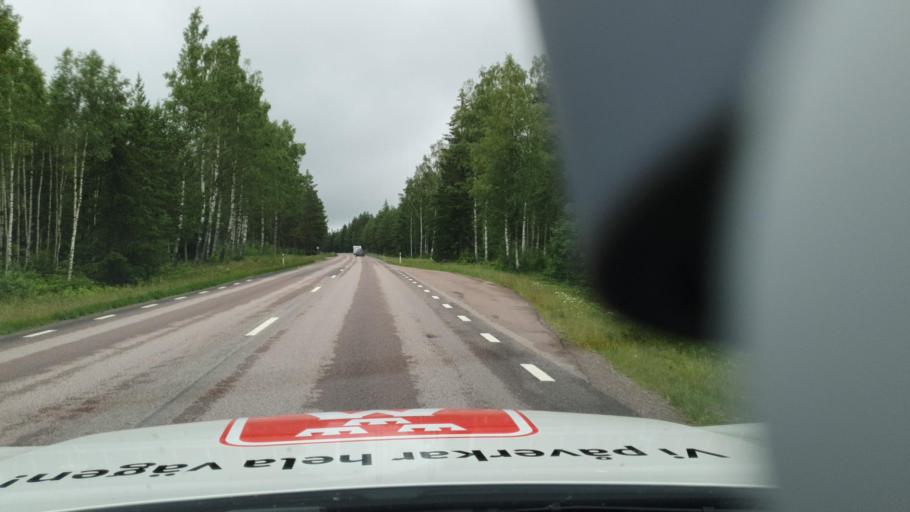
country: SE
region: Vaermland
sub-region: Kristinehamns Kommun
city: Bjorneborg
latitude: 59.1885
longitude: 14.1813
